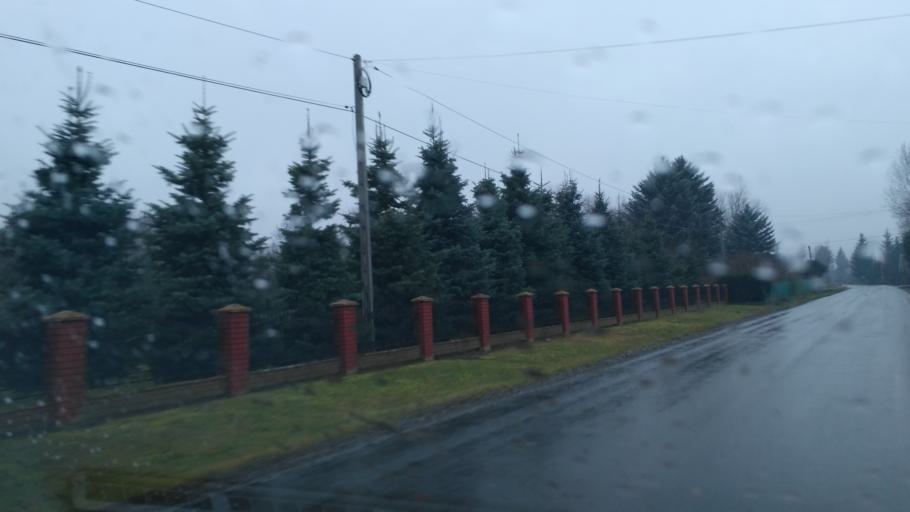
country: PL
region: Subcarpathian Voivodeship
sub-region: Powiat lancucki
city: Krzemienica
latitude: 50.0827
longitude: 22.1542
